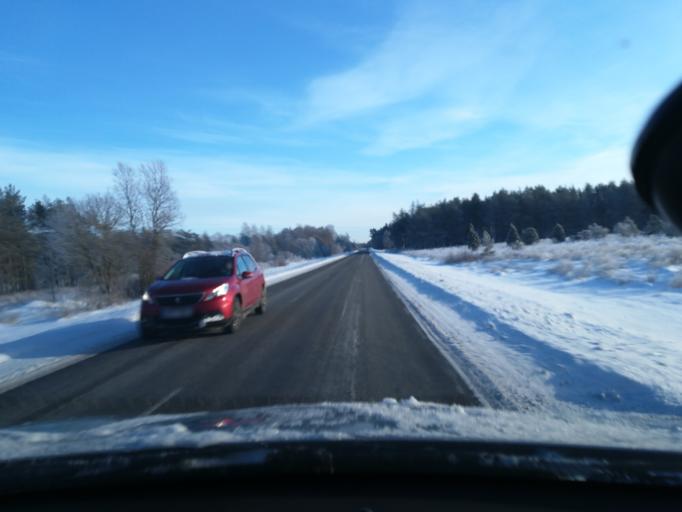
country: EE
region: Harju
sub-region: Keila linn
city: Keila
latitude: 59.3865
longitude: 24.4236
